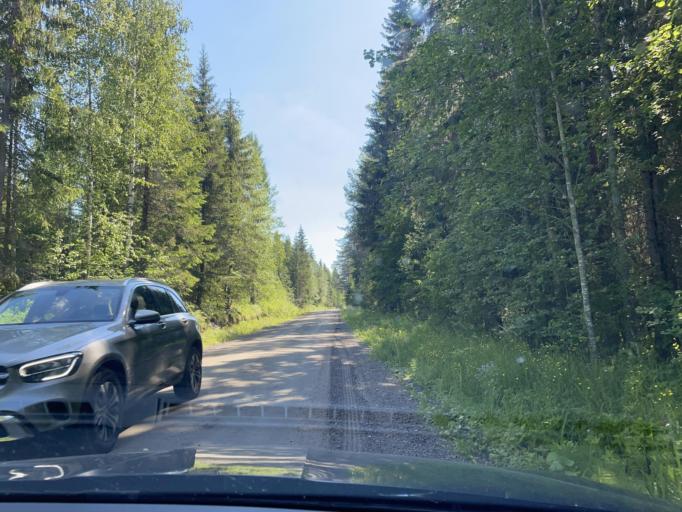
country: FI
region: Central Finland
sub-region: Saarijaervi-Viitasaari
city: Viitasaari
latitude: 63.2527
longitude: 25.9172
